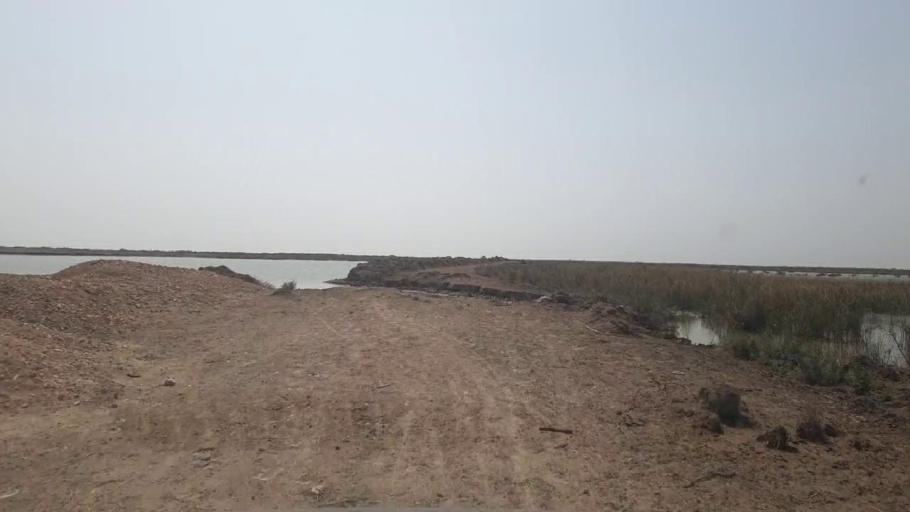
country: PK
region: Sindh
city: Jati
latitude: 24.3717
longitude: 68.6038
